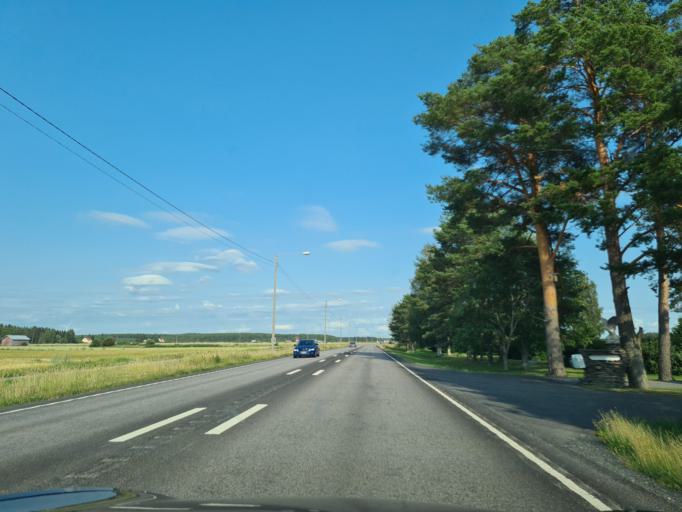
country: FI
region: Ostrobothnia
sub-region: Kyroenmaa
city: Laihia
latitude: 62.9962
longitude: 21.9263
